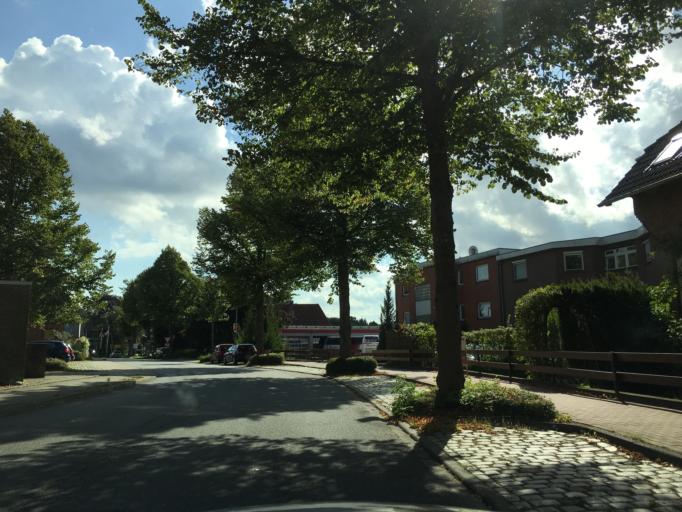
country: DE
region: Schleswig-Holstein
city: Krokau
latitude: 54.3949
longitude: 10.3700
